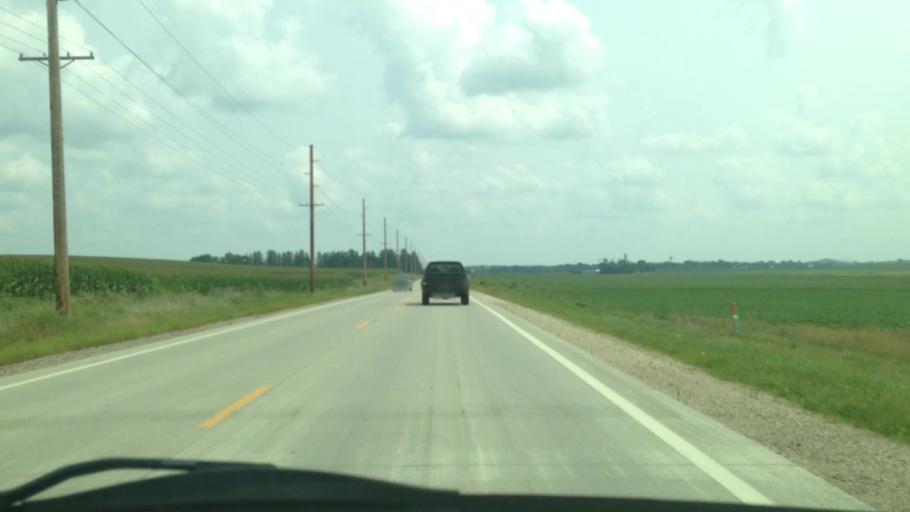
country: US
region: Minnesota
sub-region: Wabasha County
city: Elgin
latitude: 44.1367
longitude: -92.2922
